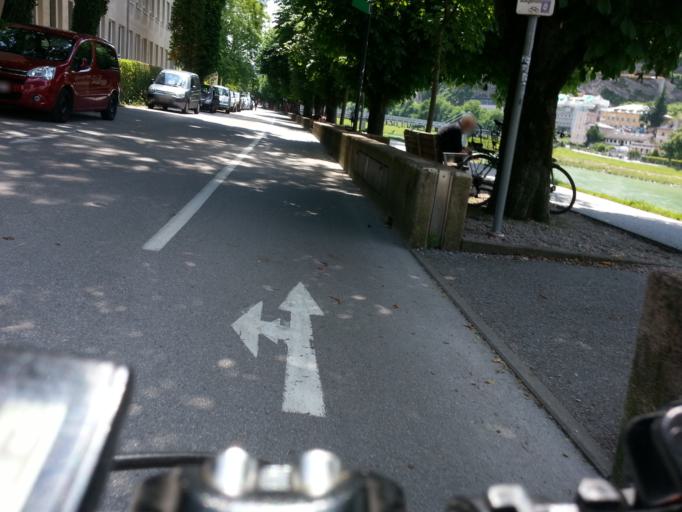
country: AT
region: Salzburg
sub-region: Salzburg Stadt
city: Salzburg
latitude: 47.8071
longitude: 13.0379
